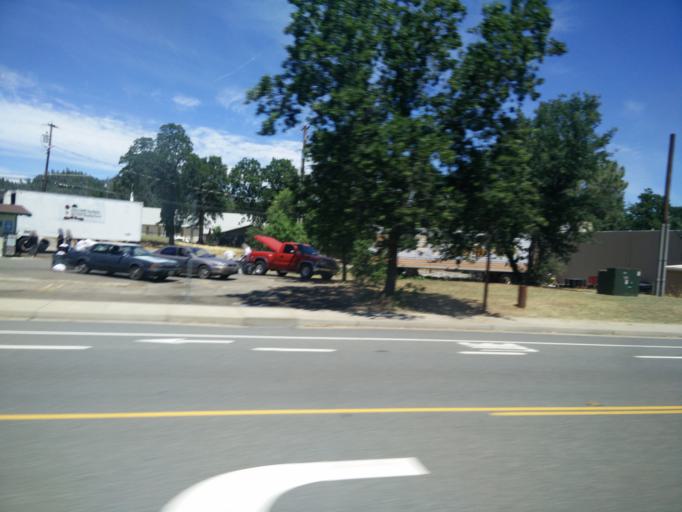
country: US
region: California
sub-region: Shasta County
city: Shasta Lake
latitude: 40.6805
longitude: -122.3651
